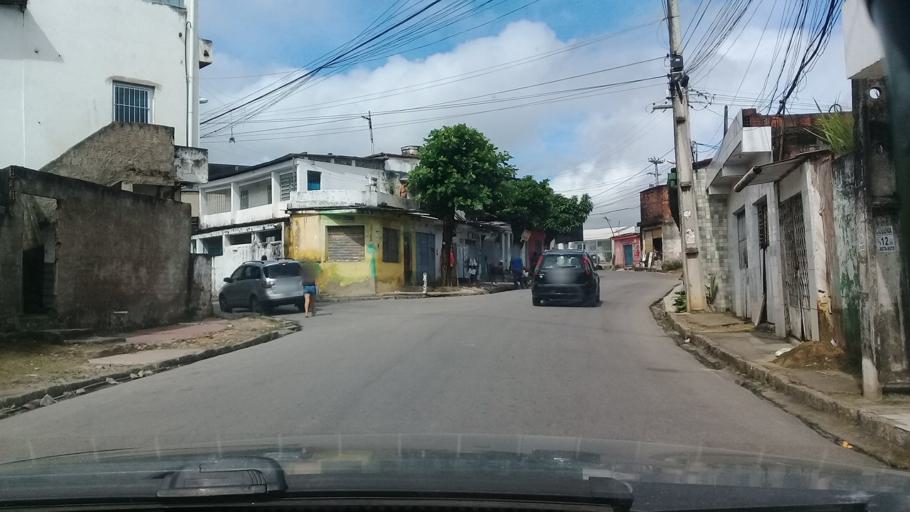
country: BR
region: Pernambuco
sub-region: Jaboatao Dos Guararapes
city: Jaboatao dos Guararapes
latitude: -8.1103
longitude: -34.9635
